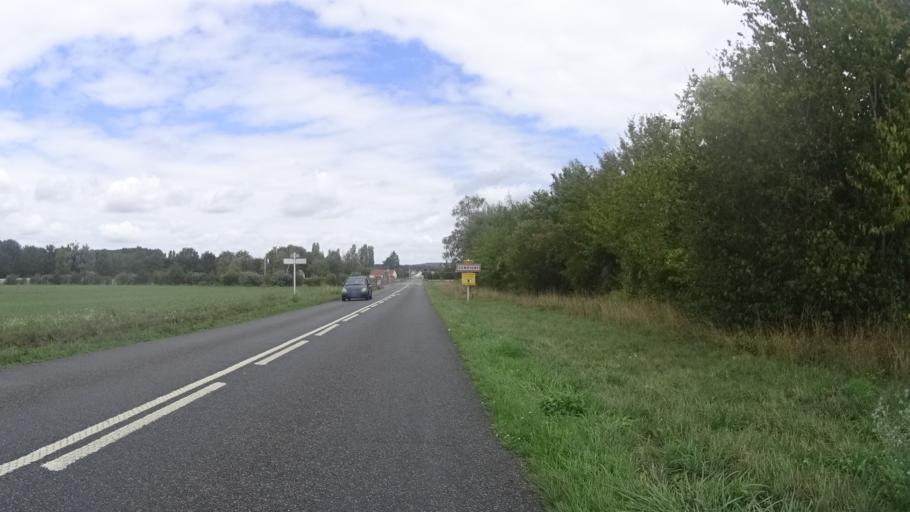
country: FR
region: Picardie
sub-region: Departement de l'Oise
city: Noyon
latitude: 49.5536
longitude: 2.9898
